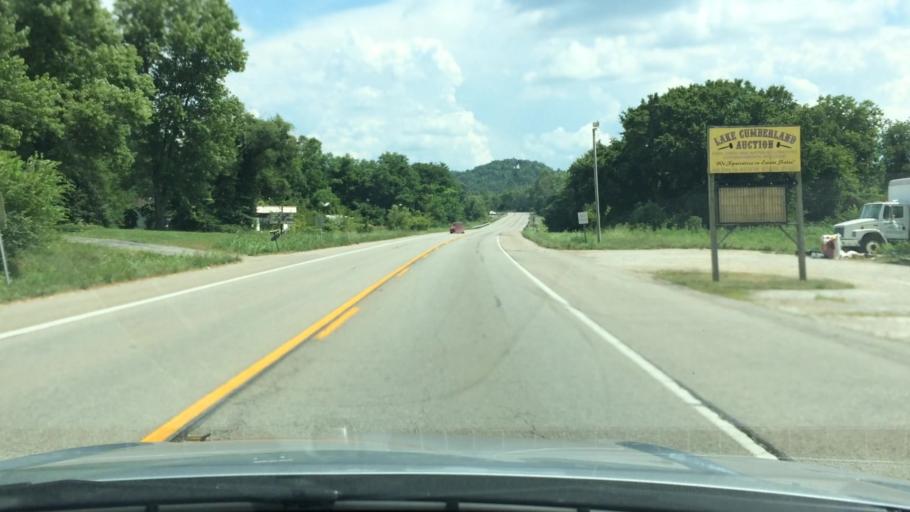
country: US
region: Kentucky
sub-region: Pulaski County
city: Somerset
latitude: 36.9611
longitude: -84.5831
